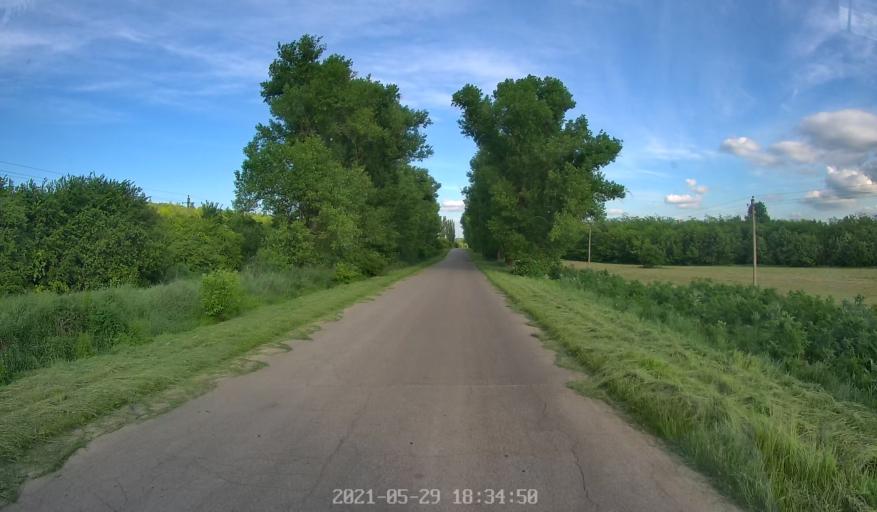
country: MD
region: Chisinau
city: Singera
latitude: 46.8114
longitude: 28.9153
